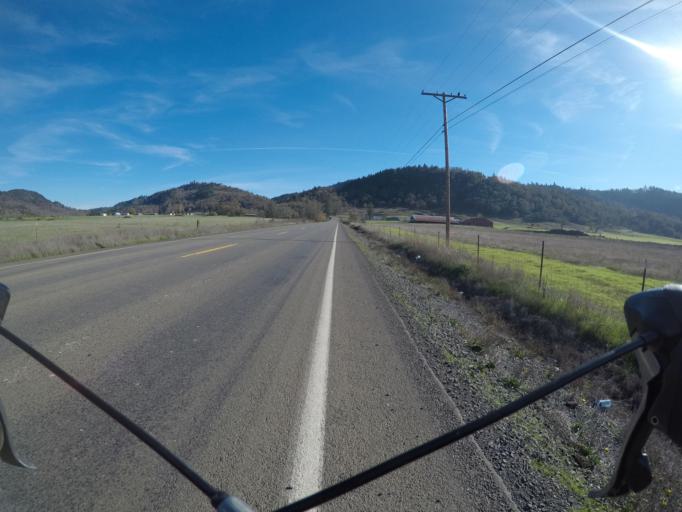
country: US
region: Oregon
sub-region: Douglas County
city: Winston
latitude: 43.1861
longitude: -123.4652
